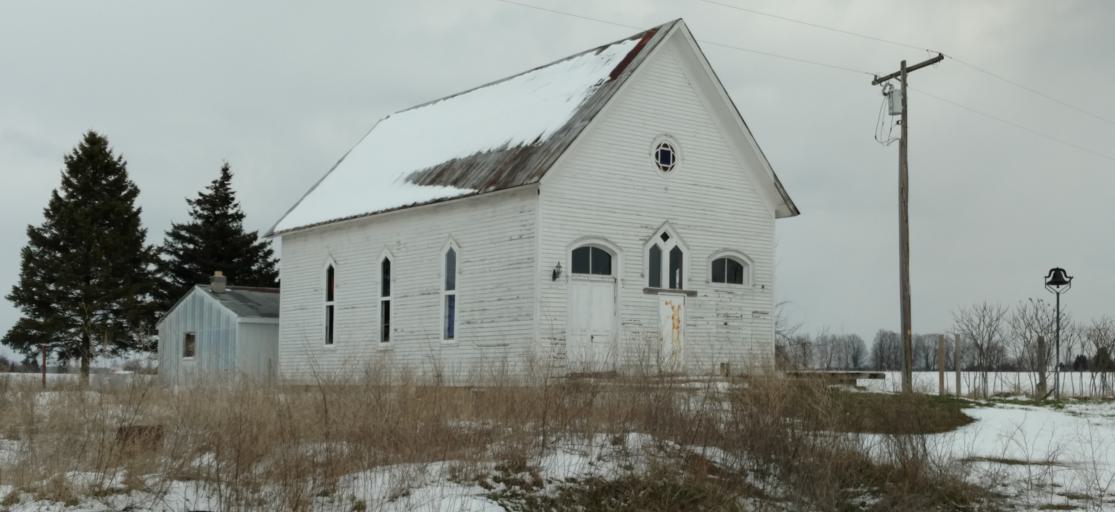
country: US
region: Michigan
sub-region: Gladwin County
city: Gladwin
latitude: 44.0379
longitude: -84.4164
